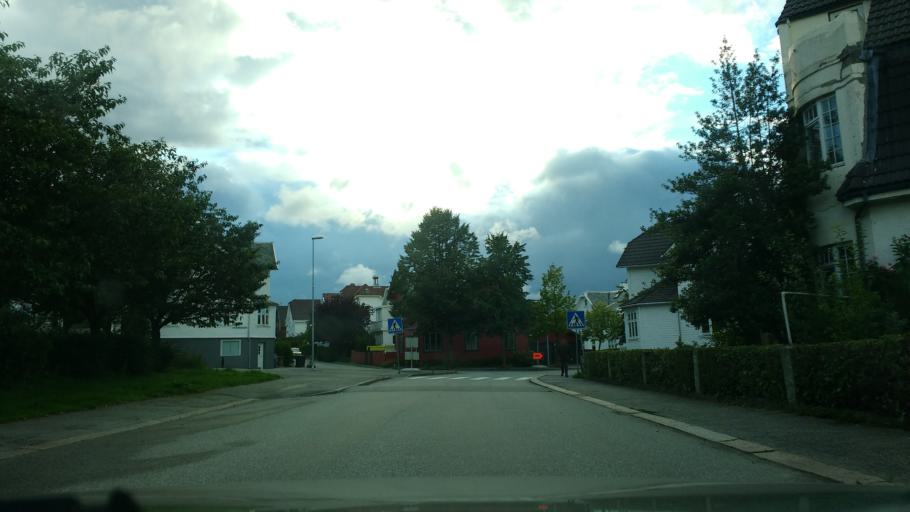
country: NO
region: Rogaland
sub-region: Stavanger
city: Stavanger
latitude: 58.9619
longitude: 5.7312
